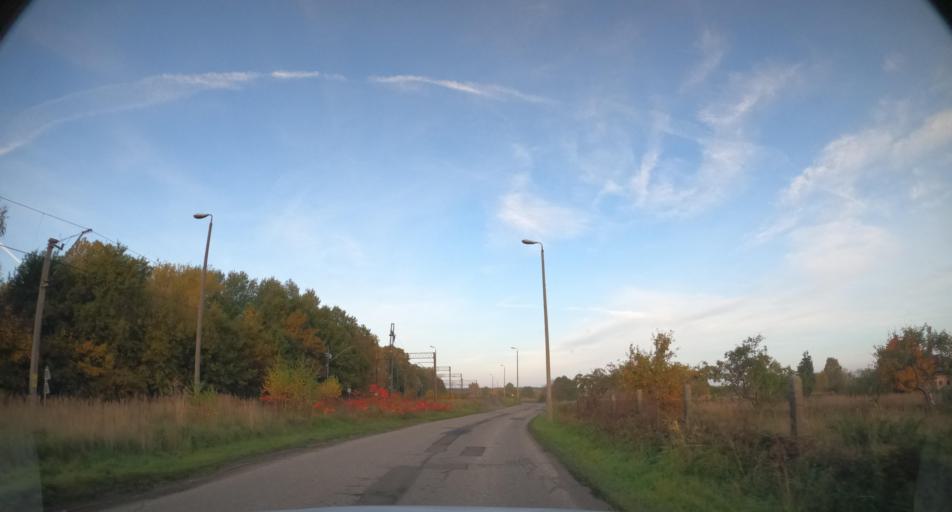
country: PL
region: West Pomeranian Voivodeship
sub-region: Powiat goleniowski
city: Stepnica
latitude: 53.6520
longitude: 14.5097
